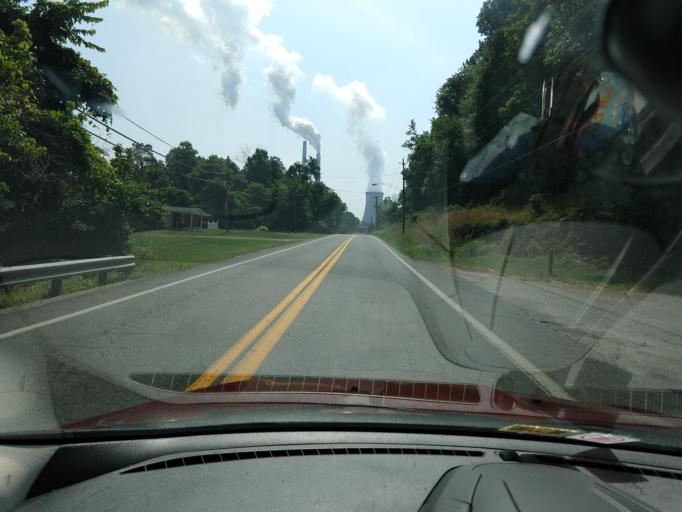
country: US
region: West Virginia
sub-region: Mason County
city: New Haven
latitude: 38.9839
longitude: -81.9557
